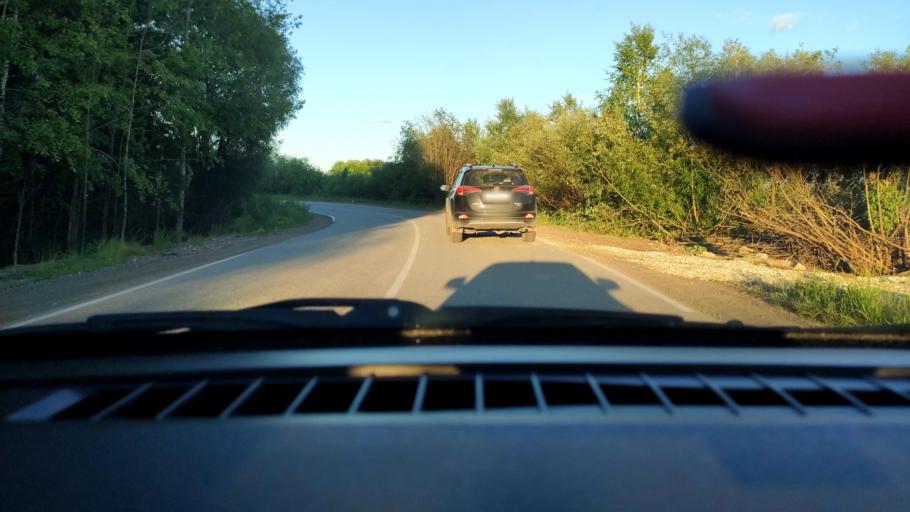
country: RU
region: Perm
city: Kultayevo
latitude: 57.9185
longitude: 55.9304
